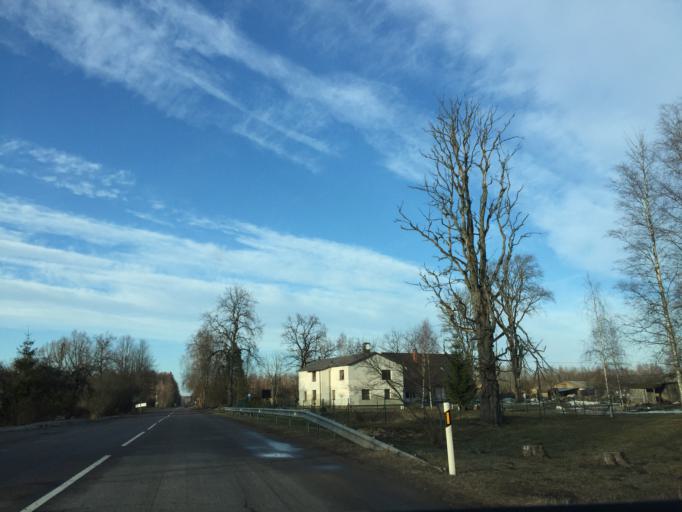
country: LV
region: Kekava
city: Balozi
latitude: 56.7350
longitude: 24.1093
